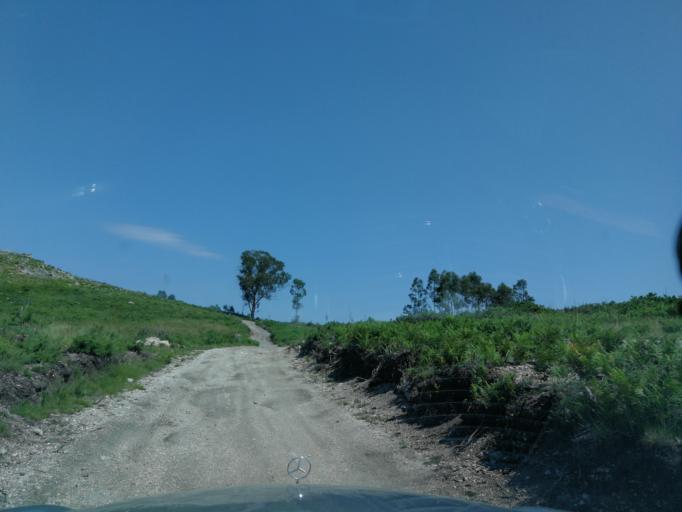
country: PT
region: Braga
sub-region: Povoa de Lanhoso
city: Povoa de Lanhoso
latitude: 41.5645
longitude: -8.3407
